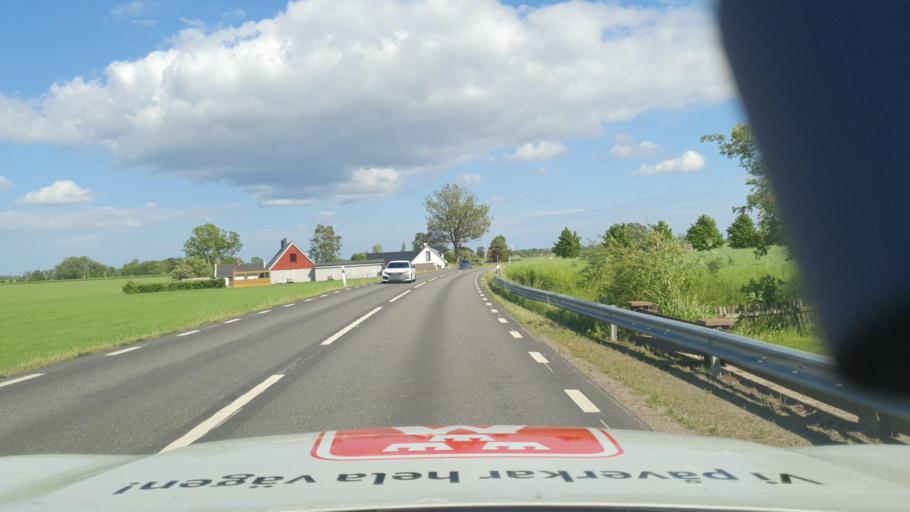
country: SE
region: Skane
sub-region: Simrishamns Kommun
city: Simrishamn
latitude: 55.5408
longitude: 14.2067
